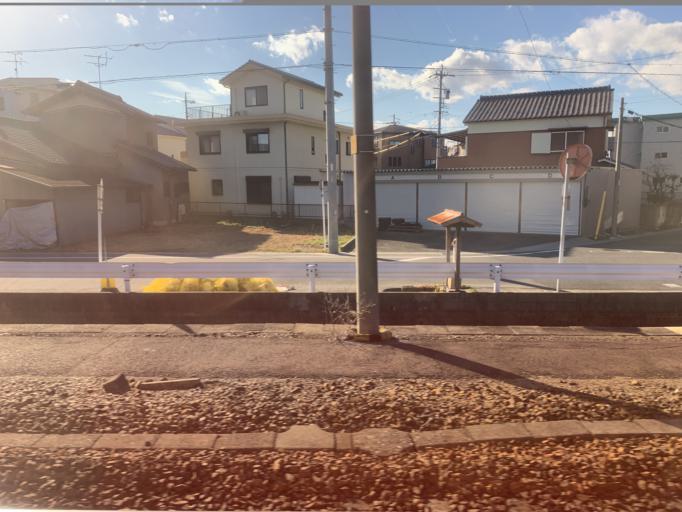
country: JP
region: Aichi
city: Inazawa
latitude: 35.2553
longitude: 136.8199
